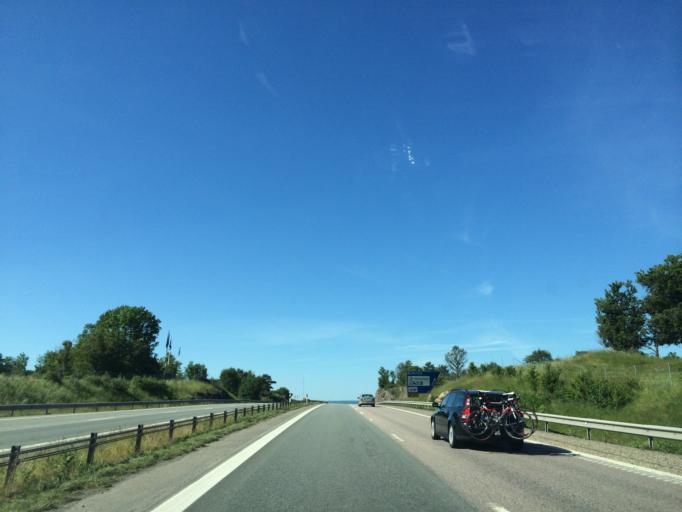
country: SE
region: Joenkoeping
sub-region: Jonkopings Kommun
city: Kaxholmen
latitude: 57.9295
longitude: 14.3253
